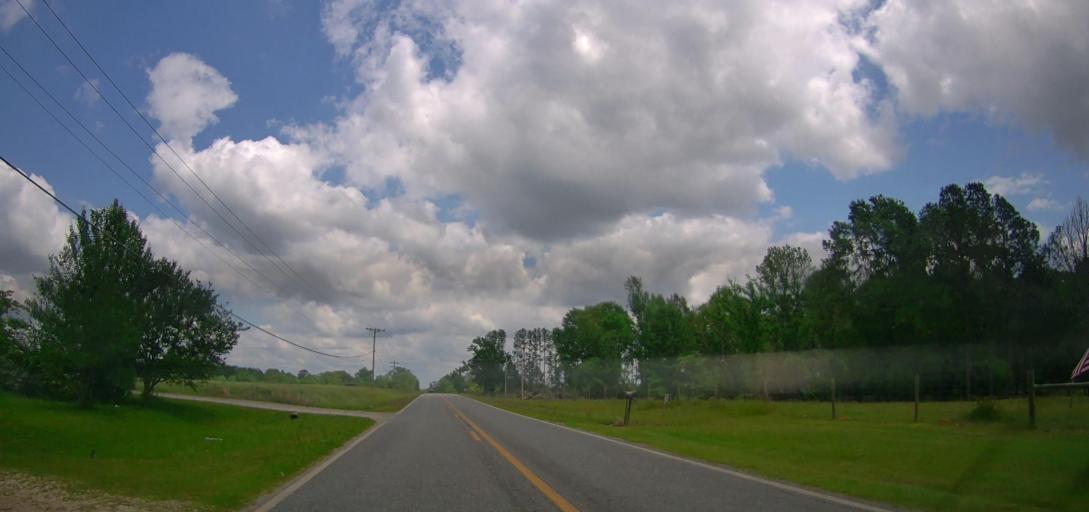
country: US
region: Georgia
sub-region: Laurens County
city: Dublin
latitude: 32.5900
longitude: -82.9381
